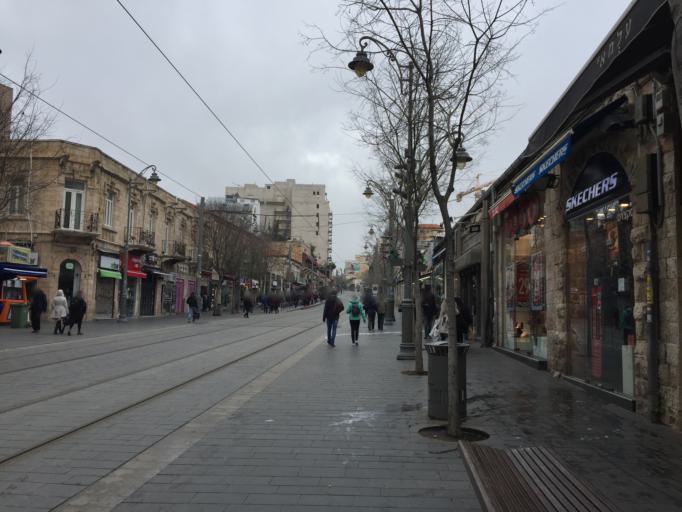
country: IL
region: Jerusalem
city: West Jerusalem
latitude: 31.7823
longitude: 35.2192
